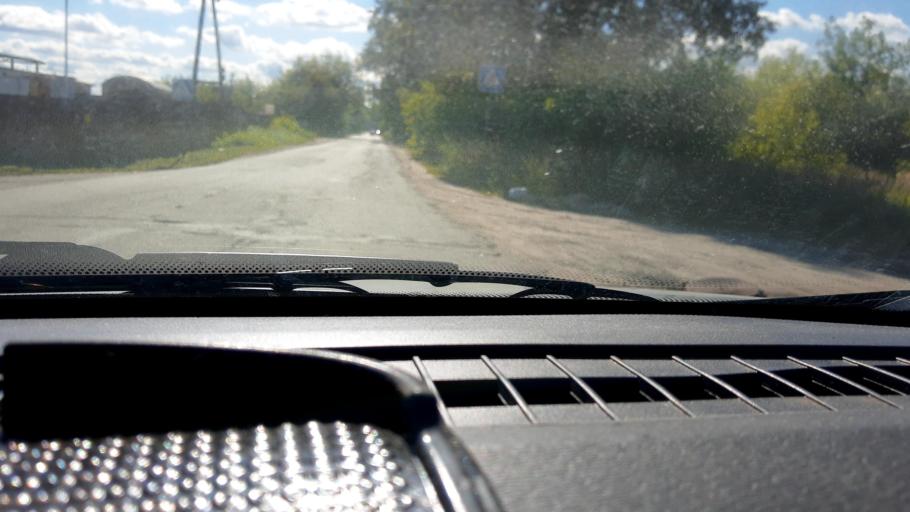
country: RU
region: Nizjnij Novgorod
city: Lukino
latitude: 56.4194
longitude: 43.6472
